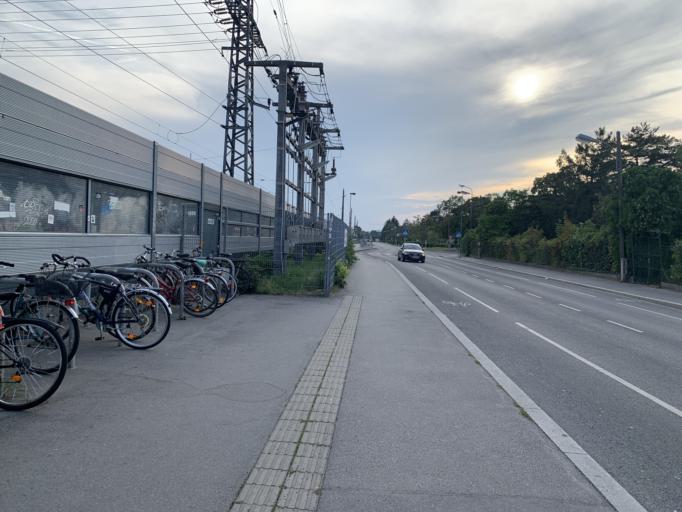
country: AT
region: Lower Austria
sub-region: Politischer Bezirk Wien-Umgebung
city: Gerasdorf bei Wien
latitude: 48.2779
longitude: 16.4502
